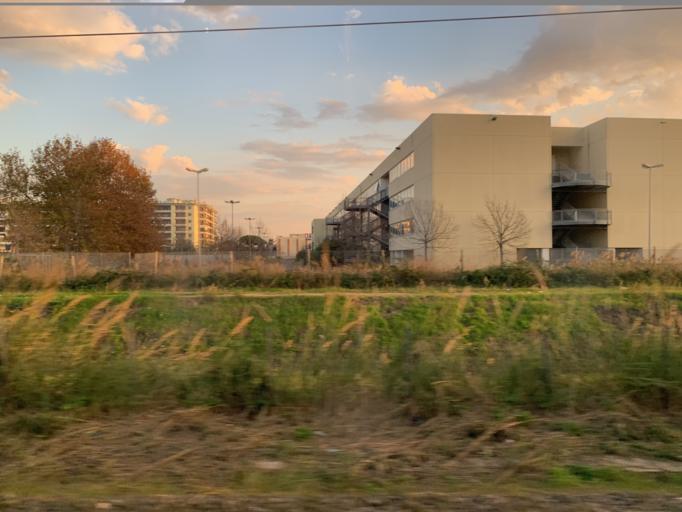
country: IT
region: Latium
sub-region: Citta metropolitana di Roma Capitale
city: Npp 23 (Parco Leonardo)
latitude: 41.8006
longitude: 12.2982
